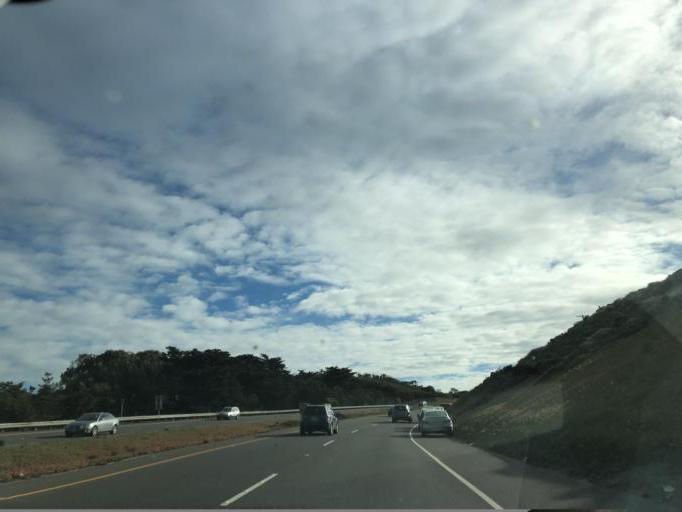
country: US
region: California
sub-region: San Mateo County
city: Broadmoor
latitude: 37.7164
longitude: -122.4991
